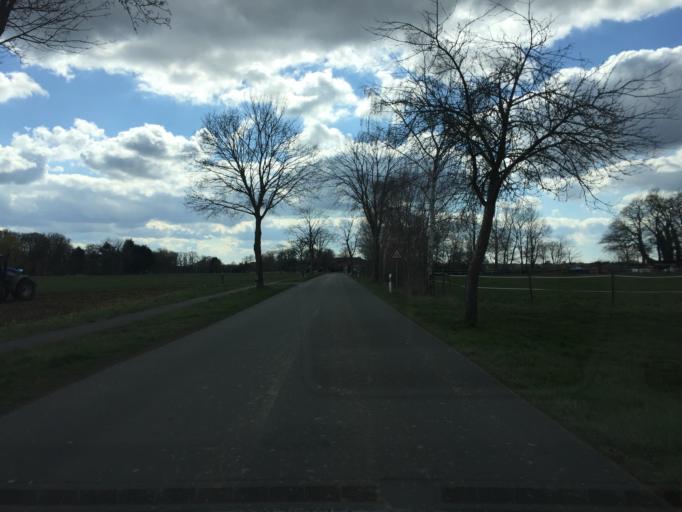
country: DE
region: Lower Saxony
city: Engeln
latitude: 52.7956
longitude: 8.9588
